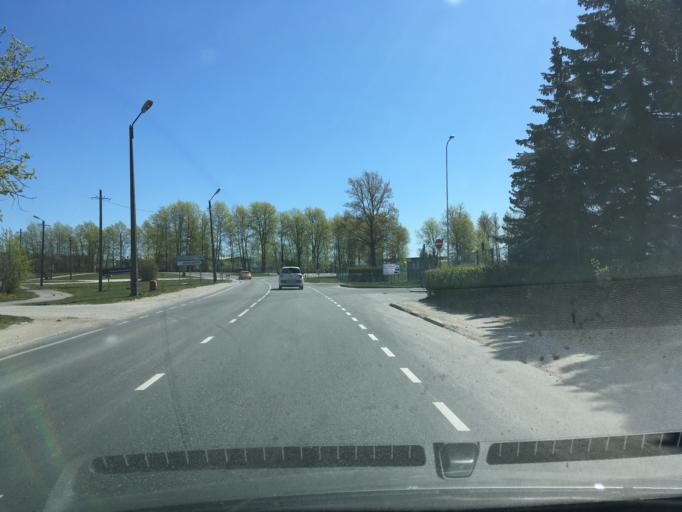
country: EE
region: Harju
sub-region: Maardu linn
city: Maardu
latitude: 59.4556
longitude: 24.9978
